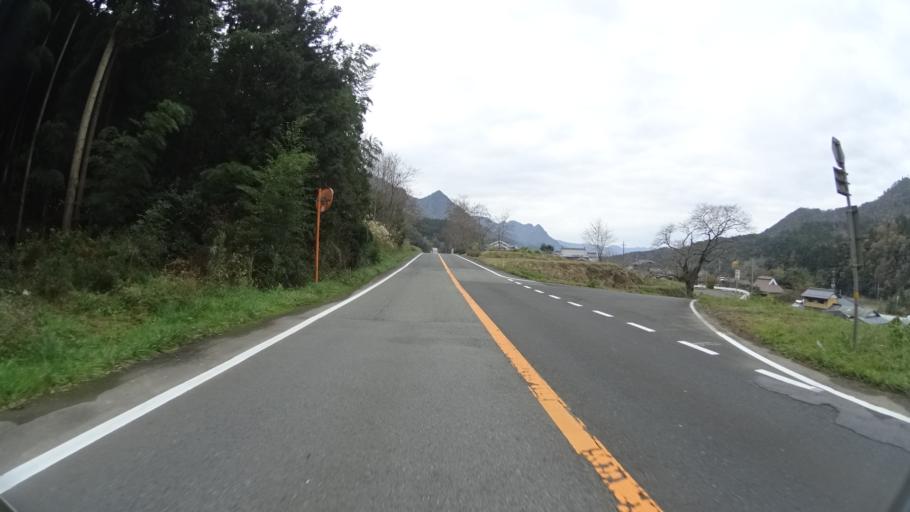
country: JP
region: Hyogo
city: Sasayama
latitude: 35.1375
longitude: 135.2008
